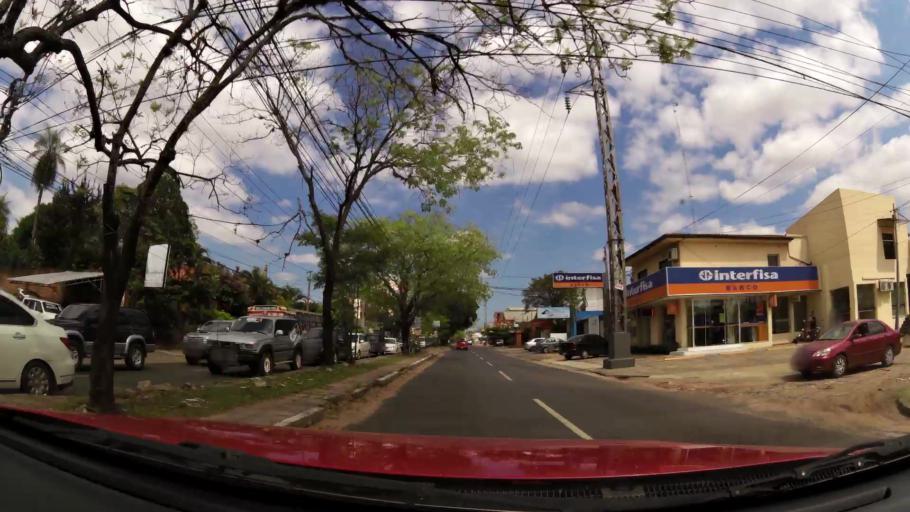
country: PY
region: Central
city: Fernando de la Mora
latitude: -25.3087
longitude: -57.5325
